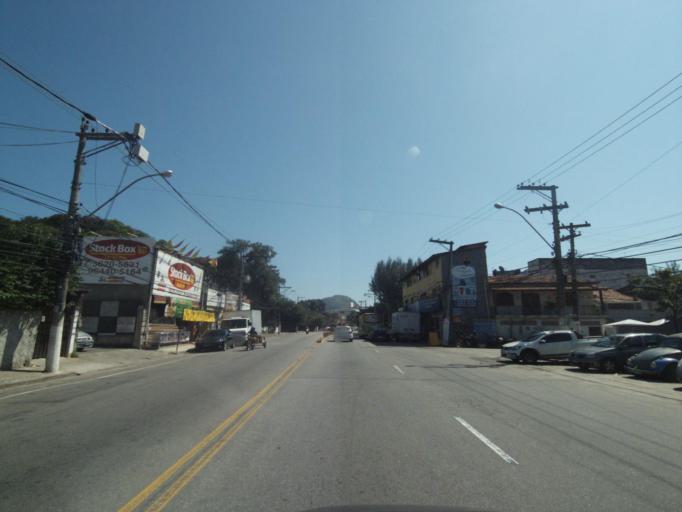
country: BR
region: Rio de Janeiro
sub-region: Niteroi
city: Niteroi
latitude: -22.9055
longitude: -43.0531
